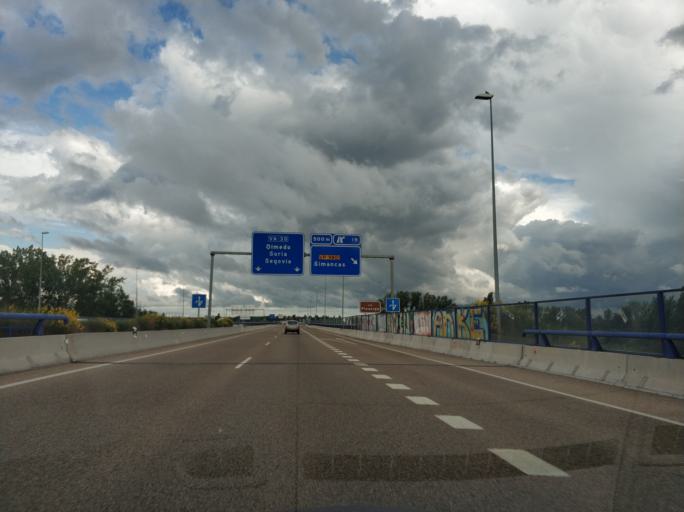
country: ES
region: Castille and Leon
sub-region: Provincia de Valladolid
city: Arroyo
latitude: 41.6165
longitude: -4.7758
